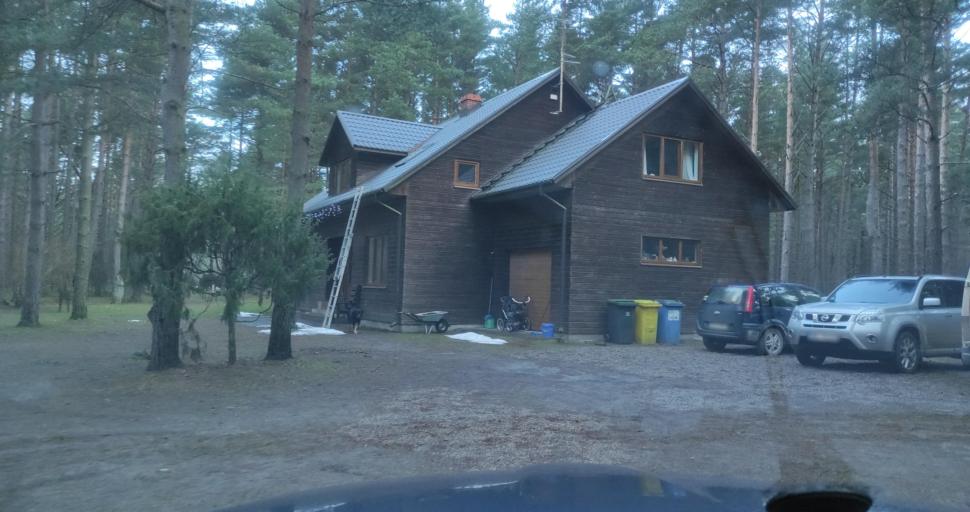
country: LV
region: Pavilostas
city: Pavilosta
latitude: 56.7811
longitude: 21.0656
